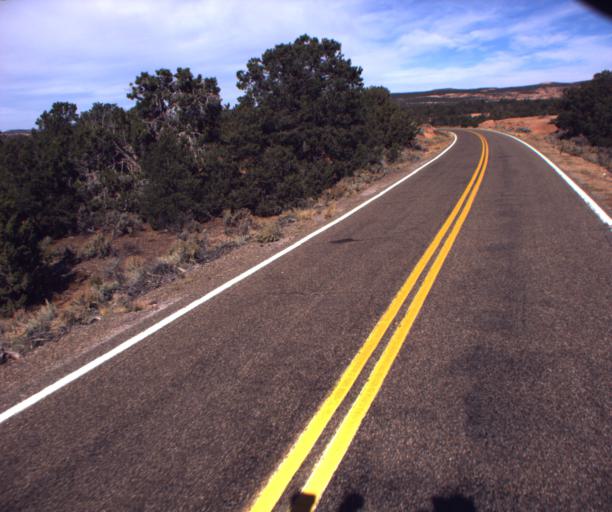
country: US
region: Arizona
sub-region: Navajo County
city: Kayenta
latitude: 36.6002
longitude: -110.4968
